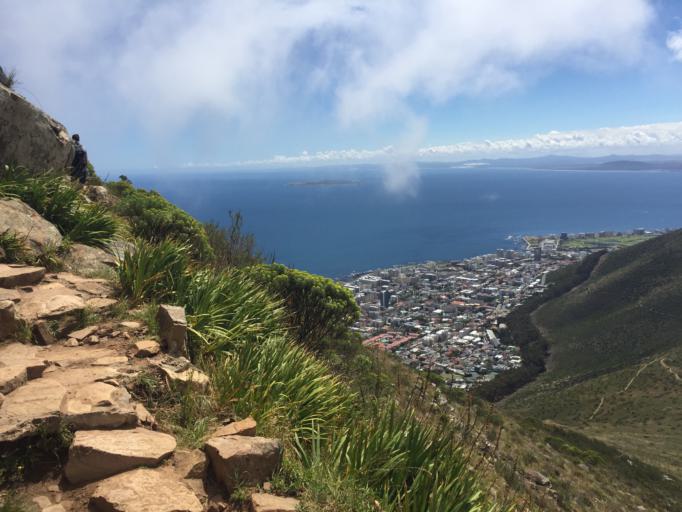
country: ZA
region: Western Cape
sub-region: City of Cape Town
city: Cape Town
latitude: -33.9349
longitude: 18.3906
